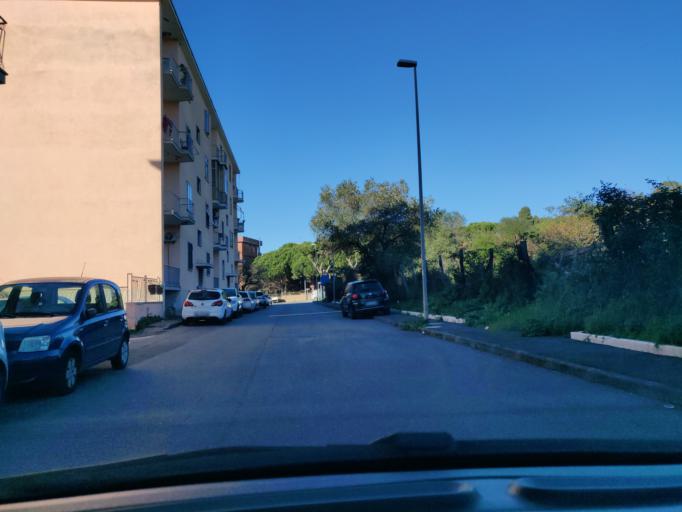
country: IT
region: Latium
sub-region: Citta metropolitana di Roma Capitale
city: Civitavecchia
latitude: 42.0961
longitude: 11.8058
